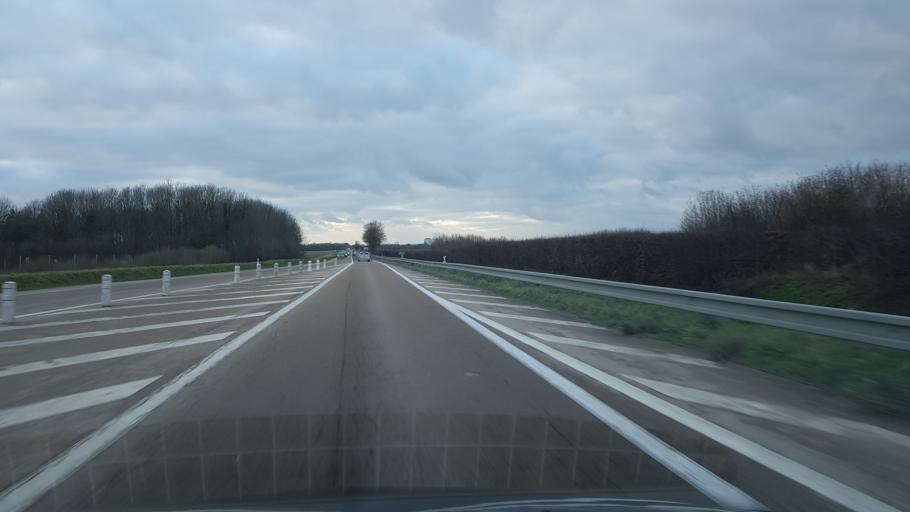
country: FR
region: Champagne-Ardenne
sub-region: Departement de la Marne
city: Connantre
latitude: 48.7413
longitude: 3.9536
